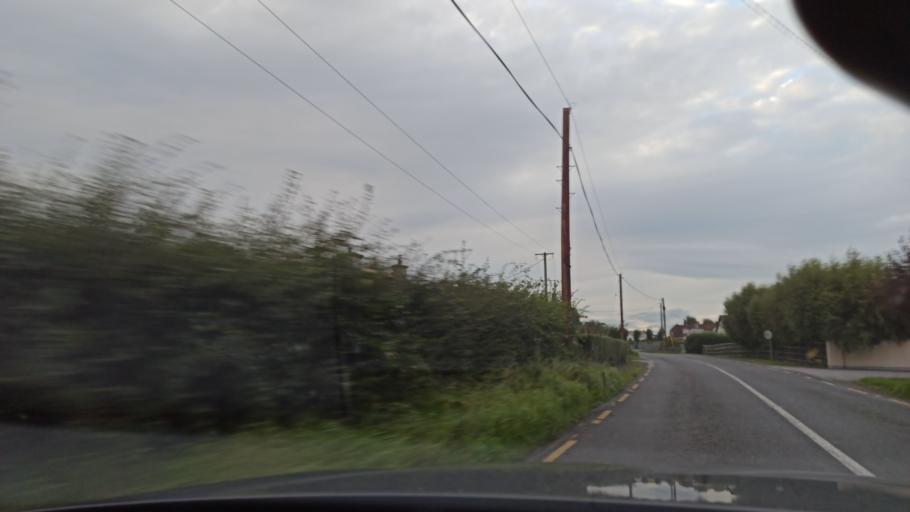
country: IE
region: Munster
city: Cashel
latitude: 52.4933
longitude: -7.8630
